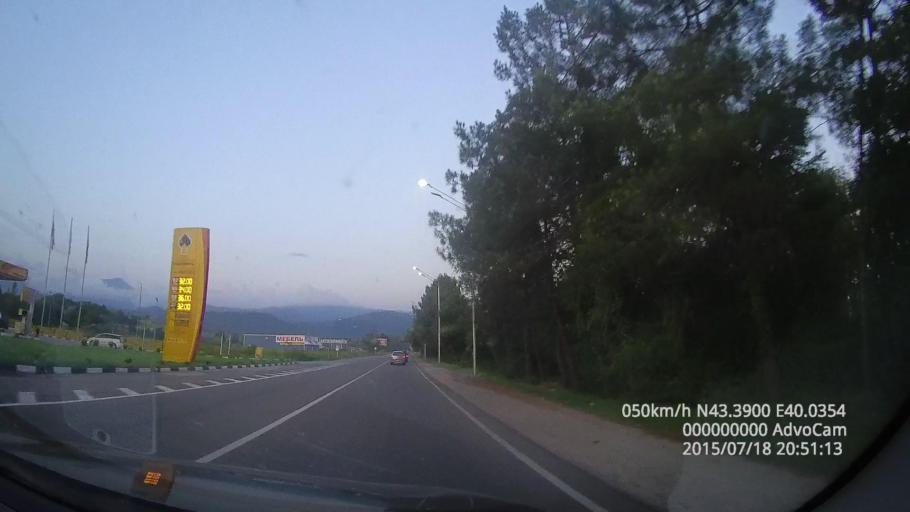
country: GE
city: Gantiadi
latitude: 43.3899
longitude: 40.0366
